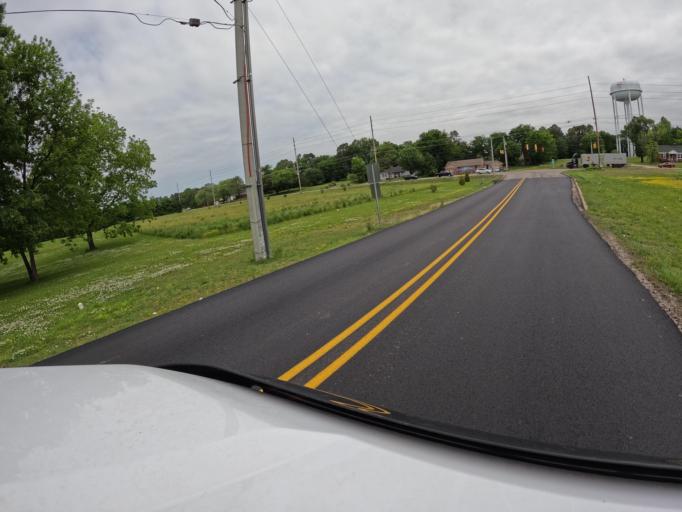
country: US
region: Mississippi
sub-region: Lee County
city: Tupelo
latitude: 34.2638
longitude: -88.7466
